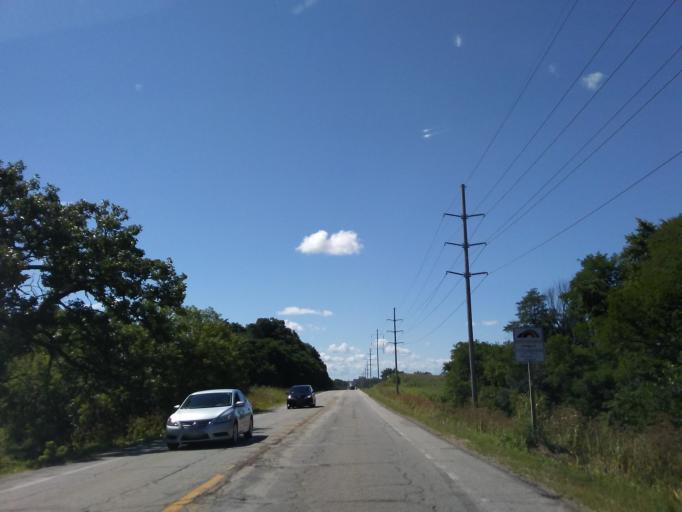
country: US
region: Wisconsin
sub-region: Dane County
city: Verona
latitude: 43.0414
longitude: -89.5329
